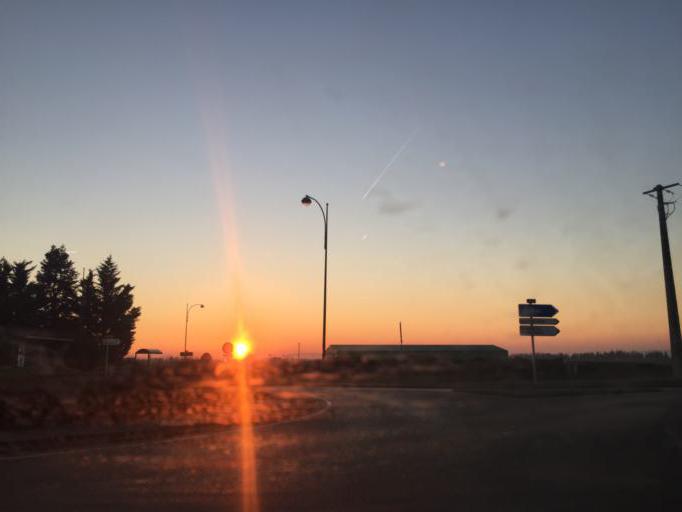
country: FR
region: Rhone-Alpes
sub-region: Departement de l'Ain
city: Balan
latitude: 45.8421
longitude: 5.1123
